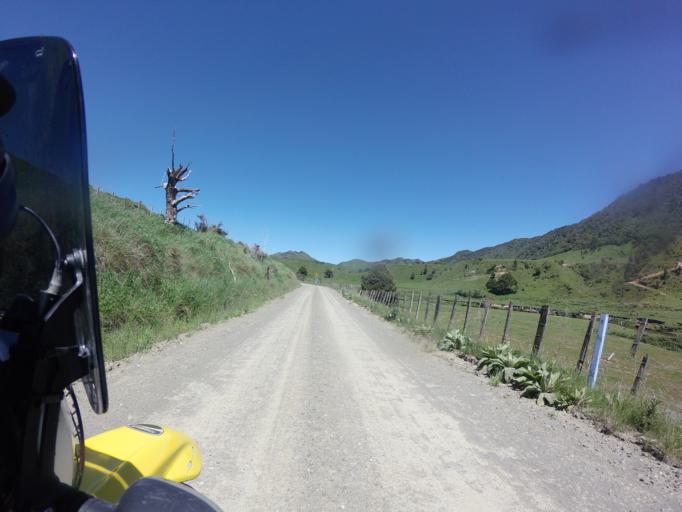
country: NZ
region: Bay of Plenty
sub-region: Opotiki District
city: Opotiki
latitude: -38.3881
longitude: 177.4614
